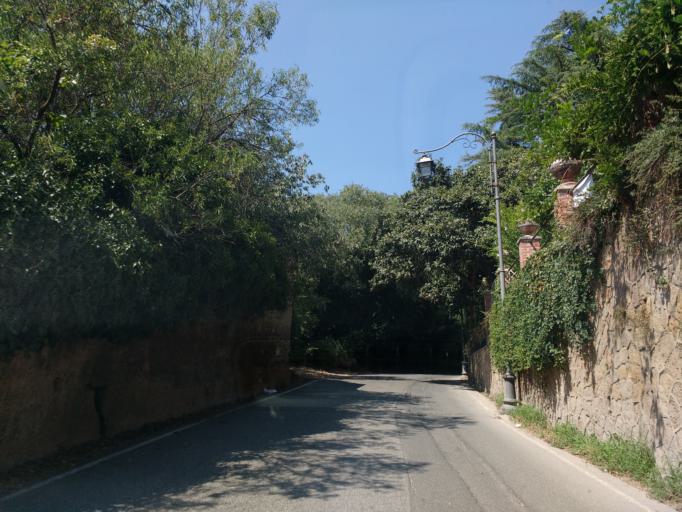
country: IT
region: Latium
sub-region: Citta metropolitana di Roma Capitale
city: Villa Adriana
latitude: 41.9475
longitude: 12.7736
